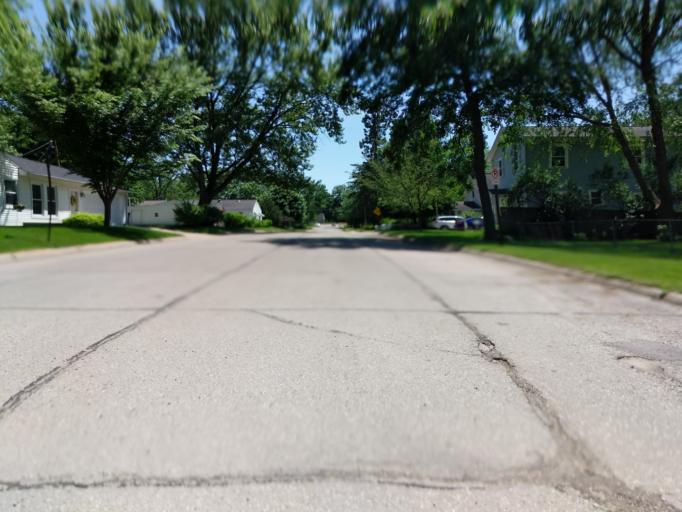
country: US
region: Iowa
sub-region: Linn County
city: Cedar Rapids
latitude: 42.0196
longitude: -91.6409
